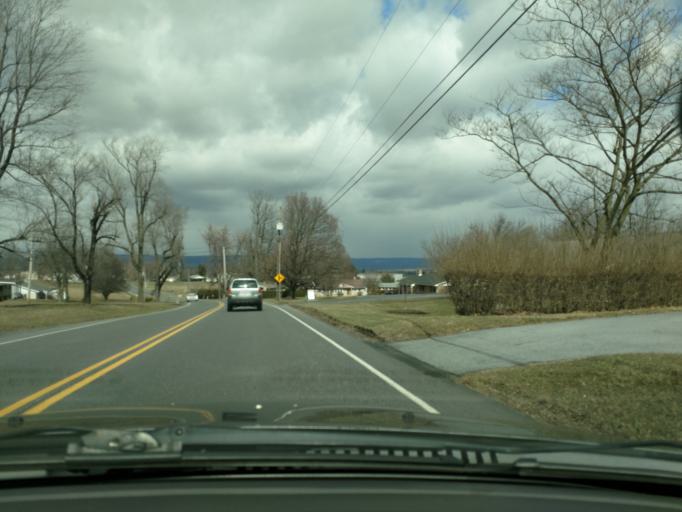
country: US
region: Pennsylvania
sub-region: Lebanon County
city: Myerstown
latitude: 40.4054
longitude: -76.3035
